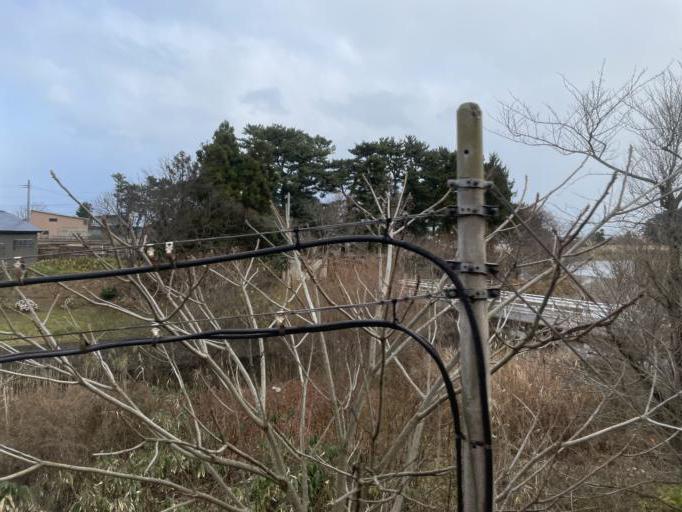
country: JP
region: Aomori
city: Aomori Shi
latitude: 41.0172
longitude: 140.6459
